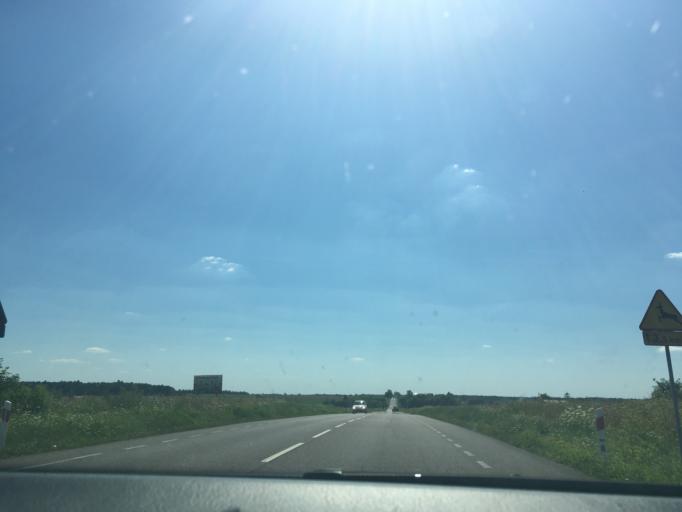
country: PL
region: Lublin Voivodeship
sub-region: Powiat janowski
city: Modliborzyce
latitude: 50.7380
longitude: 22.3506
